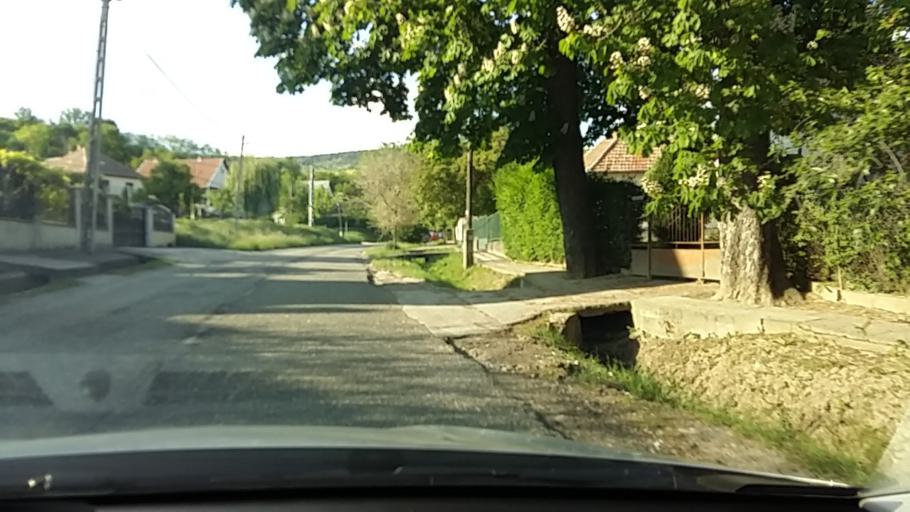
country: HU
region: Pest
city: Kosd
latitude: 47.8099
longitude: 19.2506
